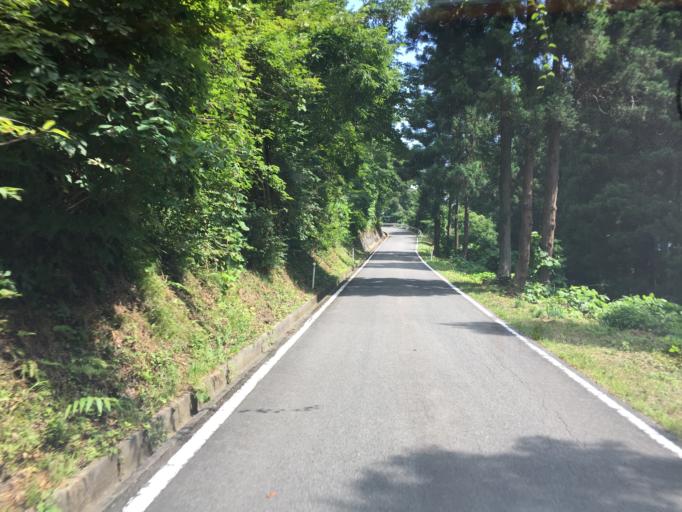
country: JP
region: Fukushima
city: Inawashiro
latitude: 37.4166
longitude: 140.1072
